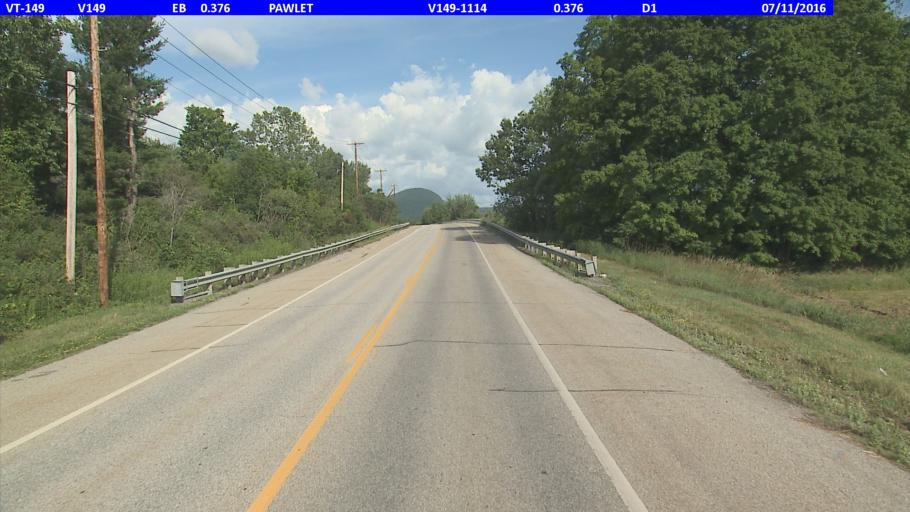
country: US
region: New York
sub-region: Washington County
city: Granville
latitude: 43.4044
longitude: -73.2439
